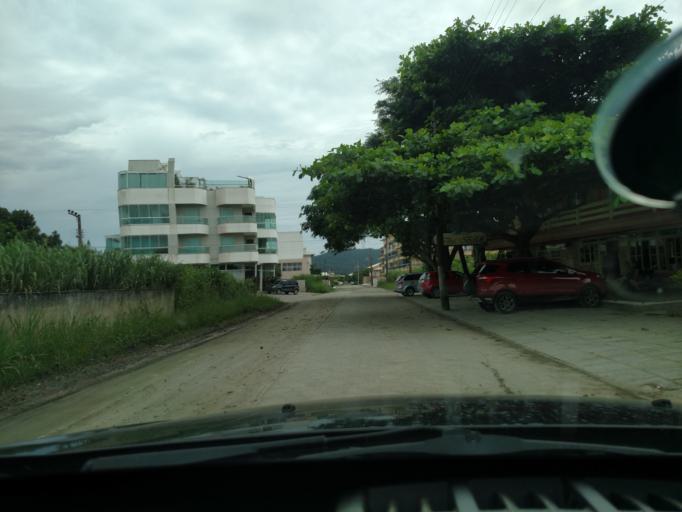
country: BR
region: Santa Catarina
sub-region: Porto Belo
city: Porto Belo
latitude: -27.1919
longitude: -48.5013
